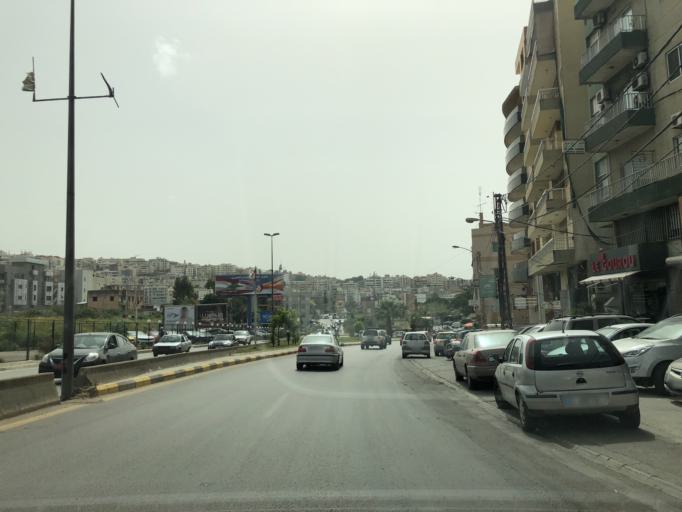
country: LB
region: Mont-Liban
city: Baabda
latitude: 33.8662
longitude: 35.5415
